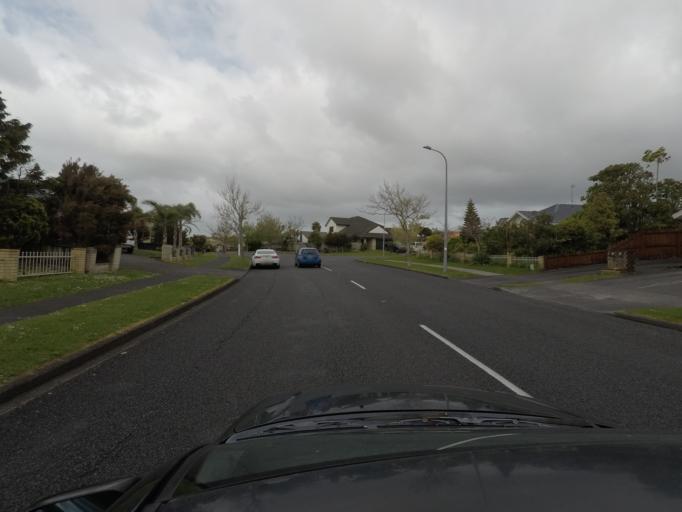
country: NZ
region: Auckland
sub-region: Auckland
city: Pakuranga
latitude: -36.9261
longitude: 174.9158
